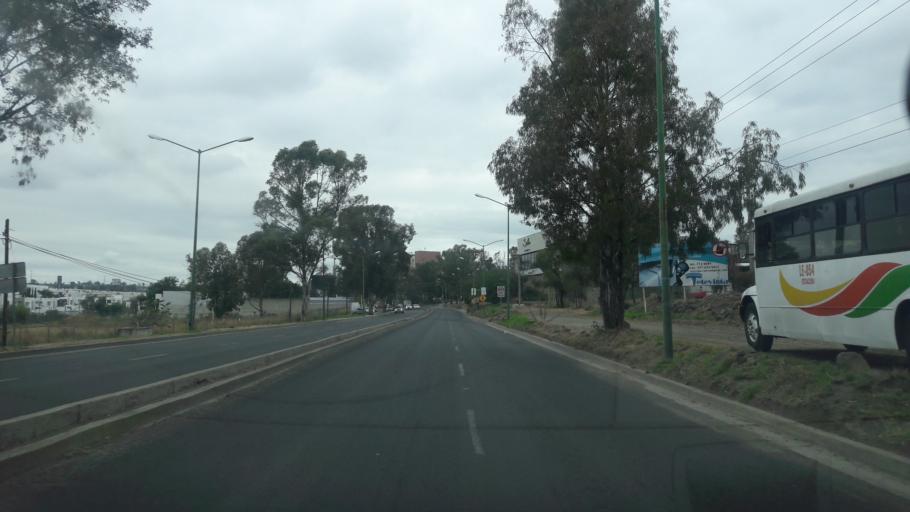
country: MX
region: Guanajuato
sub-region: Leon
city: La Ermita
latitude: 21.1659
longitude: -101.7282
